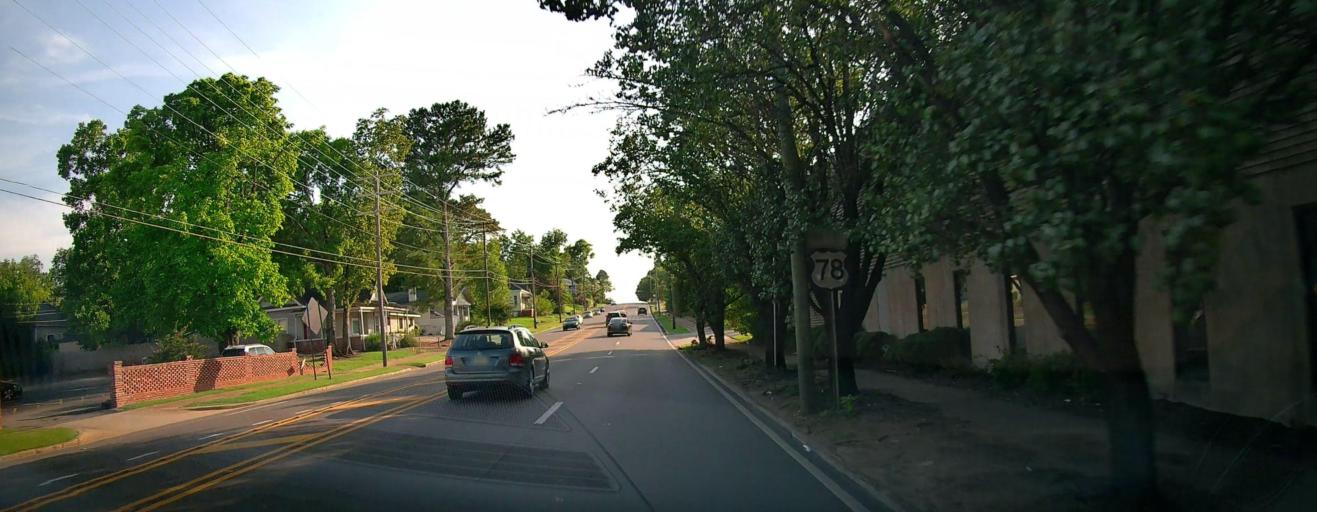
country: US
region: Alabama
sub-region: Jefferson County
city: Birmingham
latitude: 33.5235
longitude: -86.7744
